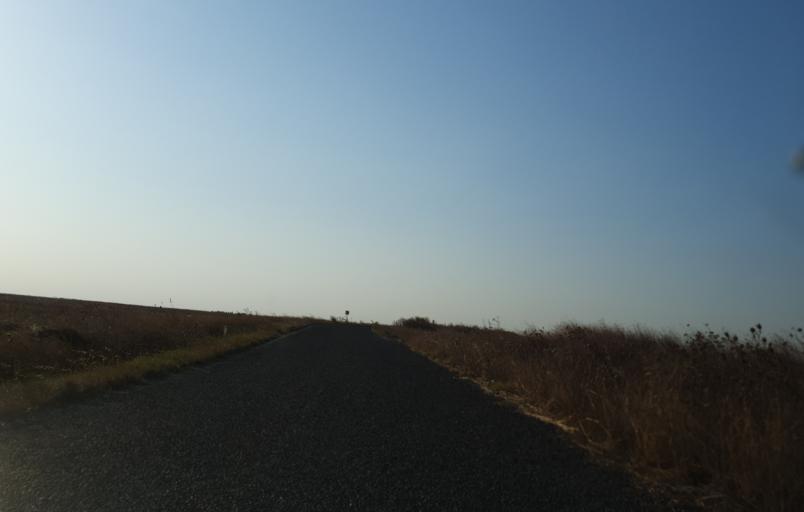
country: TR
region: Tekirdag
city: Beyazkoy
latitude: 41.4201
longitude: 27.7634
